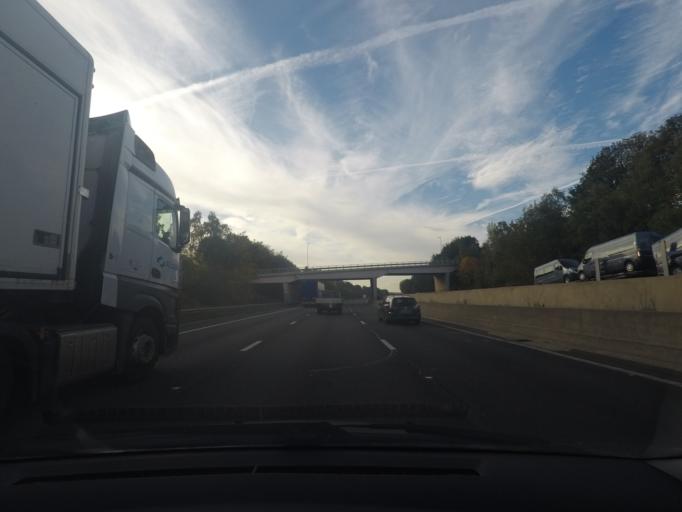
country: GB
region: England
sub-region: Barnsley
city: Darton
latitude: 53.5847
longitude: -1.5354
